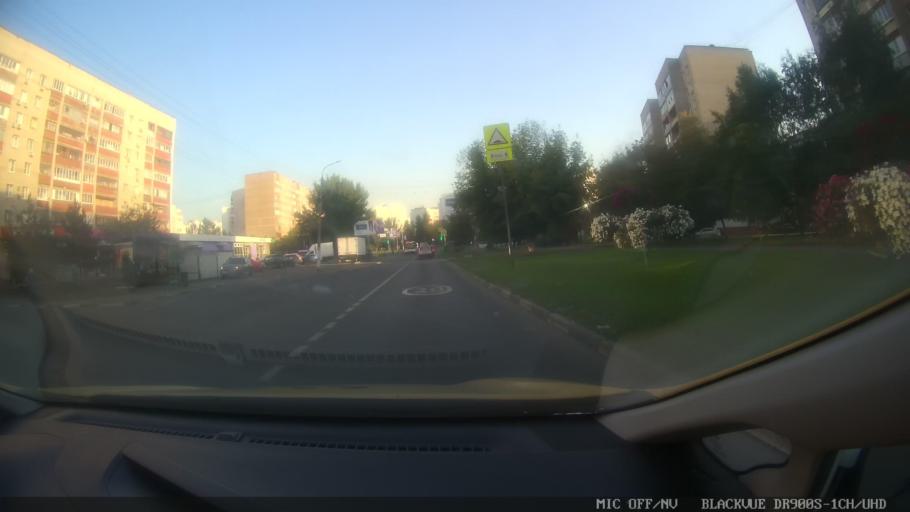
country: RU
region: Moscow
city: Nekrasovka
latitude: 55.6963
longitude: 37.9009
